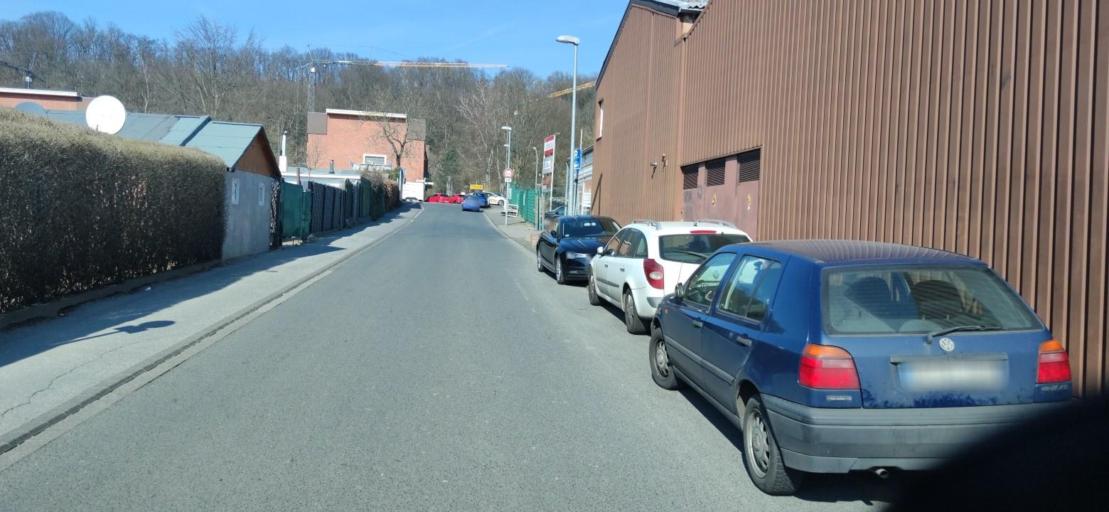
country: DE
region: North Rhine-Westphalia
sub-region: Regierungsbezirk Dusseldorf
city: Erkrath
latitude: 51.2230
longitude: 6.8710
